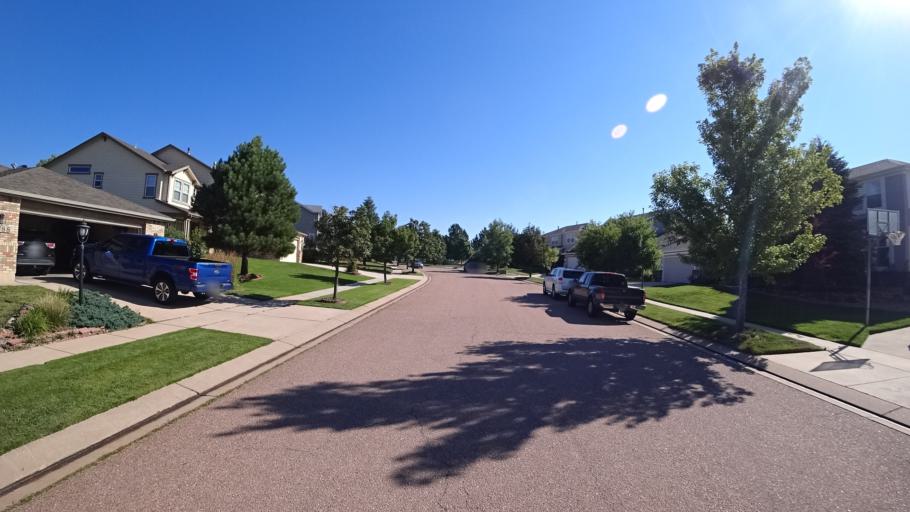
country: US
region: Colorado
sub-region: El Paso County
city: Black Forest
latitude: 38.9776
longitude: -104.7716
